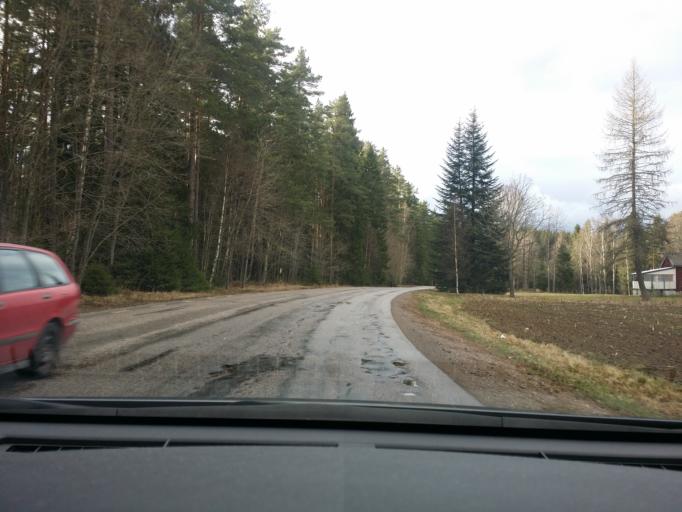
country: SE
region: Soedermanland
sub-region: Eskilstuna Kommun
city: Arla
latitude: 59.3109
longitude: 16.6813
